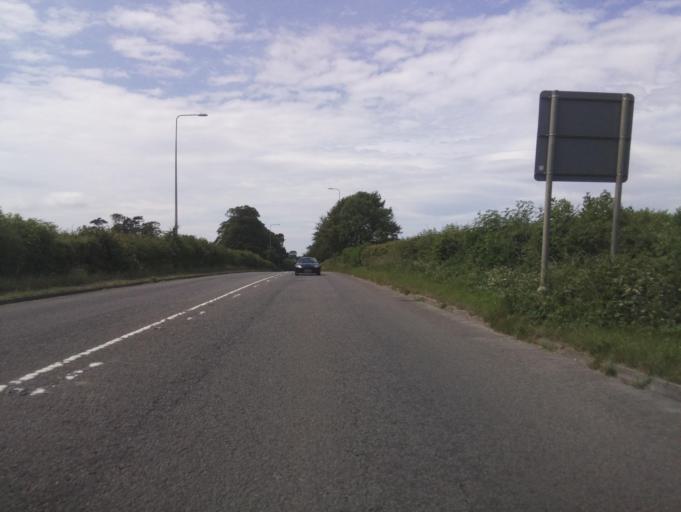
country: GB
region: Wales
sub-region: Vale of Glamorgan
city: Penllyn
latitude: 51.4674
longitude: -3.4721
